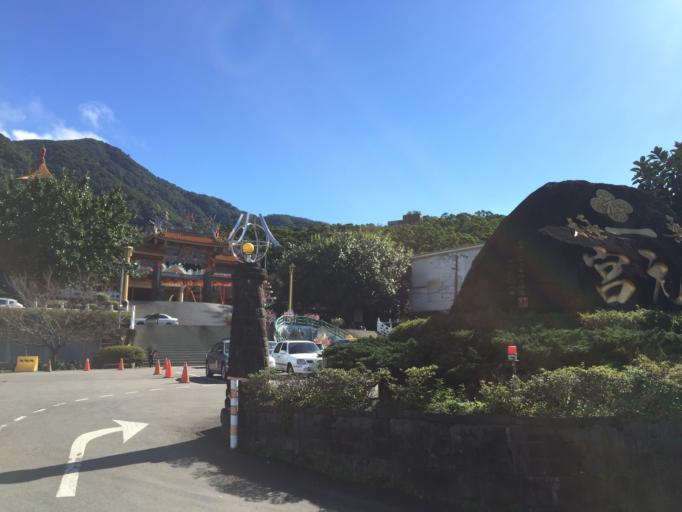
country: TW
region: Taipei
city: Taipei
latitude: 25.1871
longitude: 121.4841
